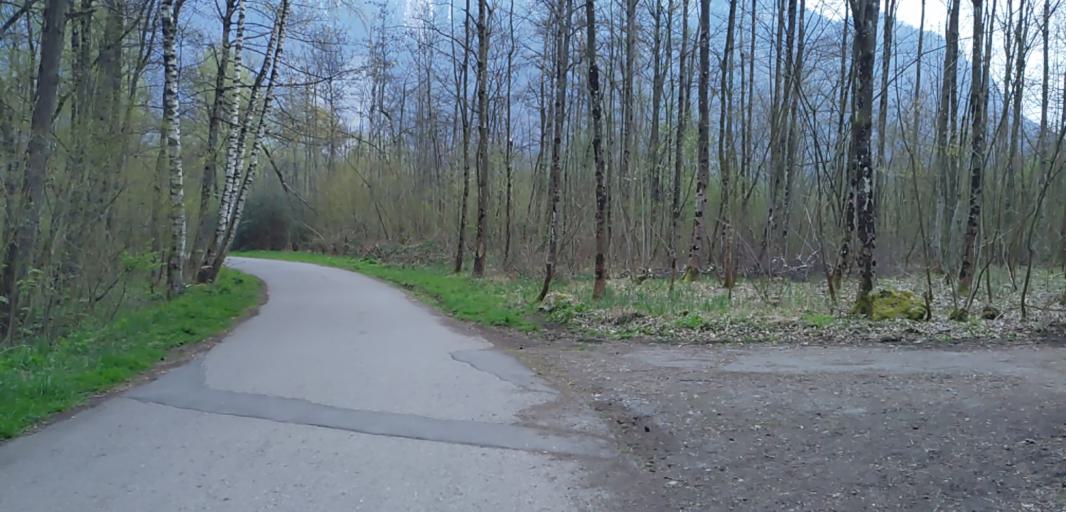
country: CH
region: Vaud
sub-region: Aigle District
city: Villeneuve
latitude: 46.3936
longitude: 6.9161
